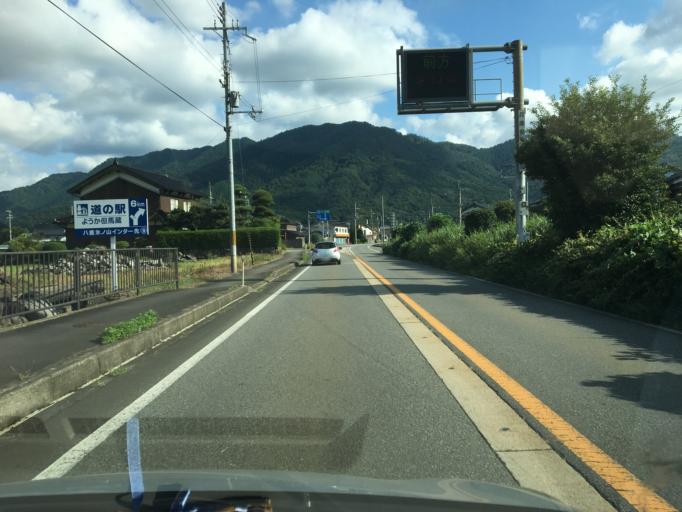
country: JP
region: Hyogo
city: Toyooka
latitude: 35.4261
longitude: 134.7889
